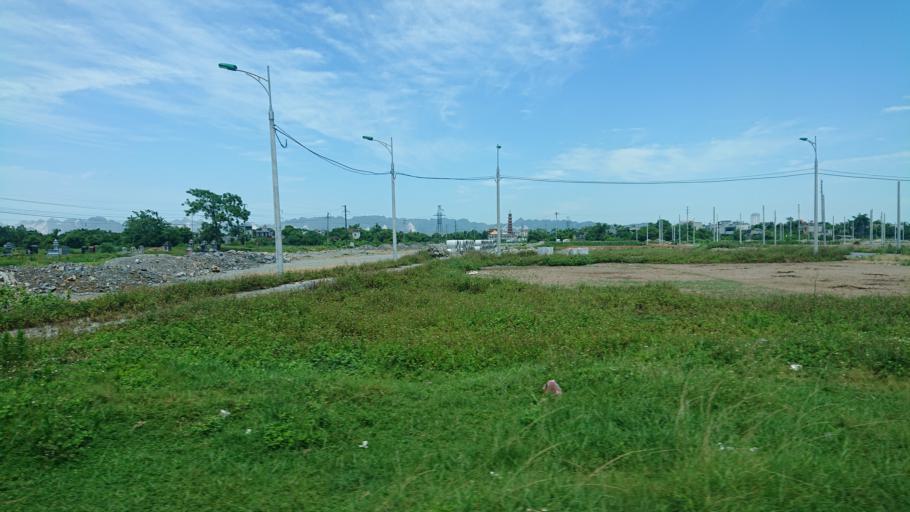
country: VN
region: Ha Nam
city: Thanh Pho Phu Ly
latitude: 20.5332
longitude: 105.9456
